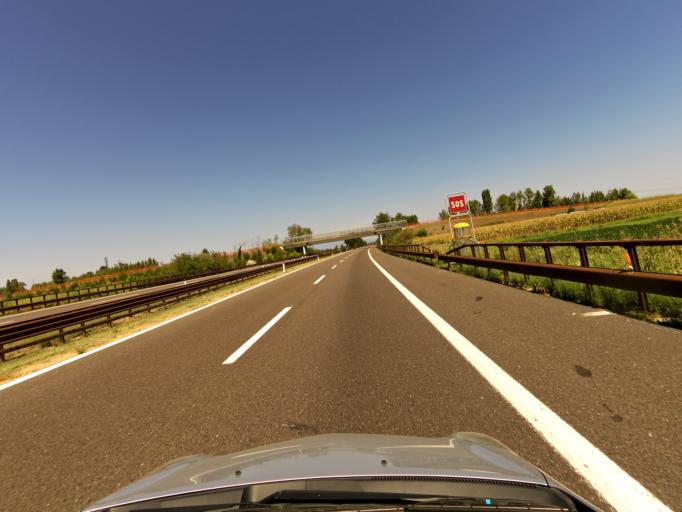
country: IT
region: Lombardy
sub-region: Provincia di Mantova
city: Mottella
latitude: 45.2023
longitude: 10.8465
